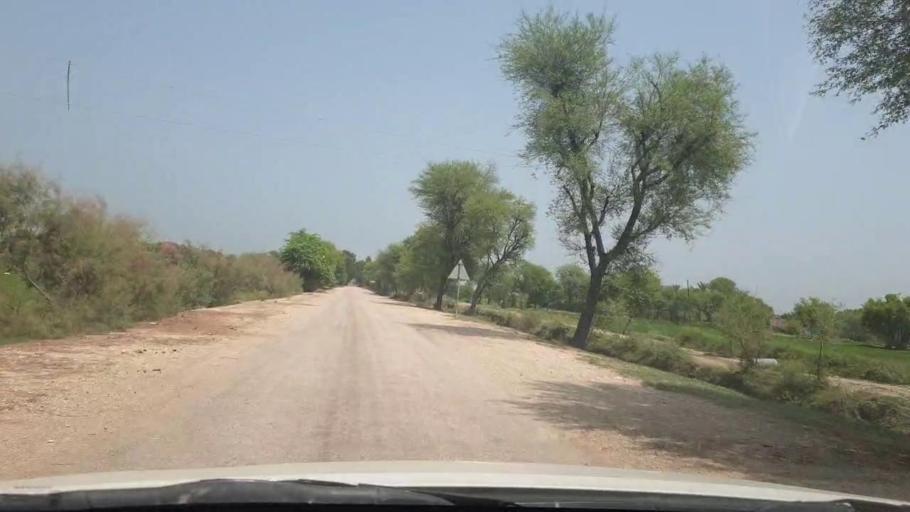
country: PK
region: Sindh
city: Rustam jo Goth
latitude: 28.0272
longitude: 68.7609
